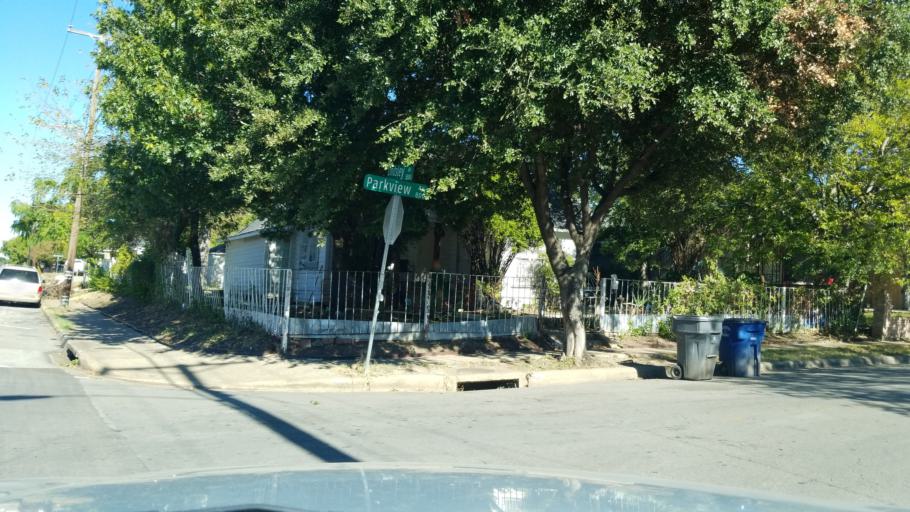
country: US
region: Texas
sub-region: Dallas County
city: Highland Park
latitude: 32.7980
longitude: -96.7492
